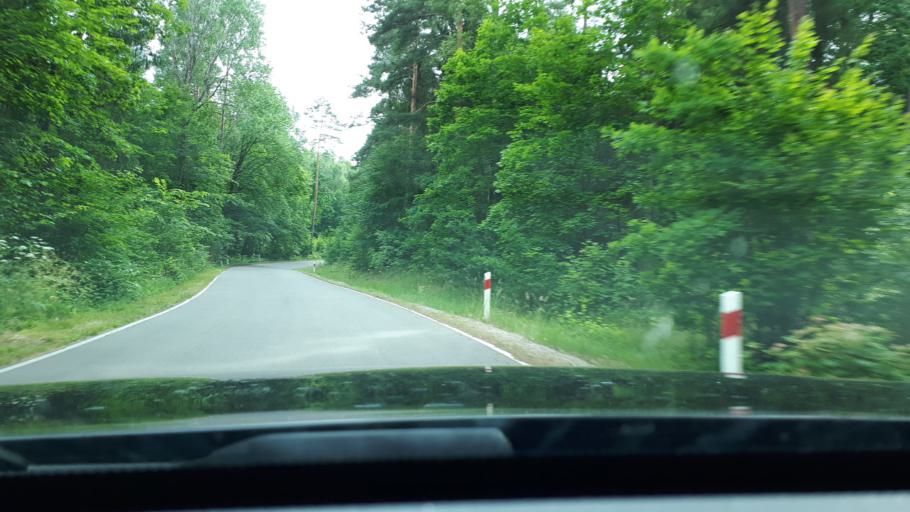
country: PL
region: Warmian-Masurian Voivodeship
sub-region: Powiat ostrodzki
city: Ostroda
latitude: 53.6844
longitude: 20.0740
